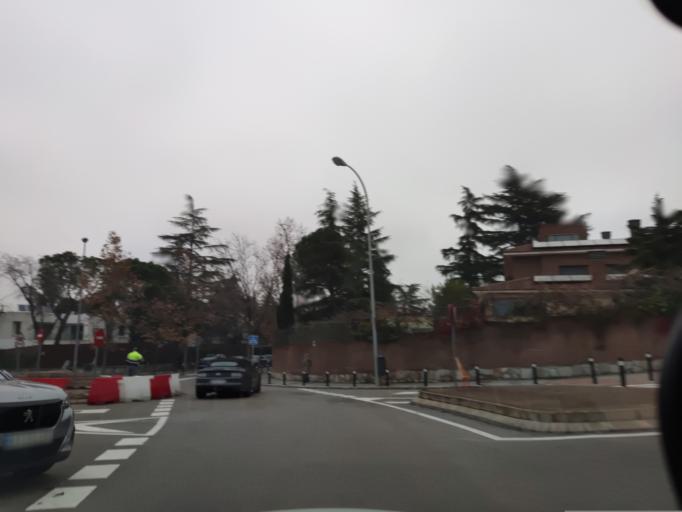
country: ES
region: Madrid
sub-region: Provincia de Madrid
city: Fuencarral-El Pardo
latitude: 40.4875
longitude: -3.7139
